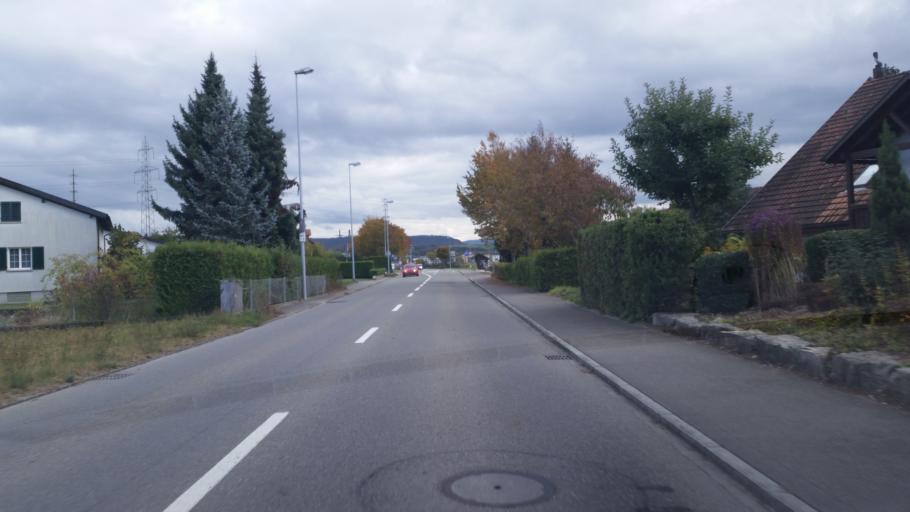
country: CH
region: Aargau
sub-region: Bezirk Zurzach
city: Klingnau
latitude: 47.5763
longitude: 8.2287
